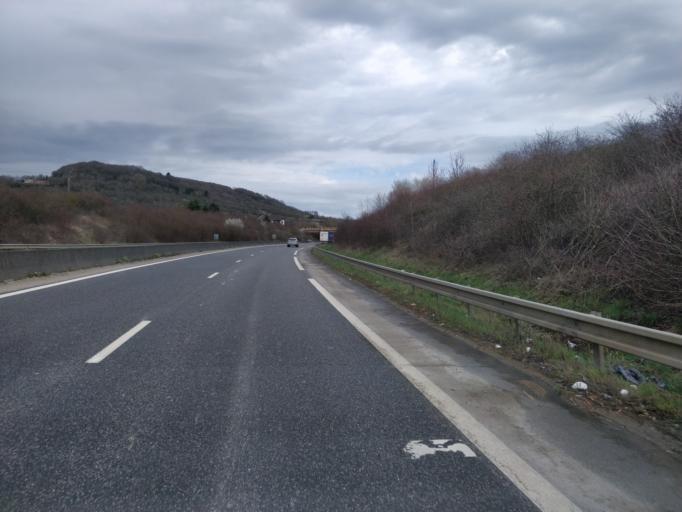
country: FR
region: Lorraine
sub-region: Departement de la Moselle
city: Vitry-sur-Orne
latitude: 49.2683
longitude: 6.1099
